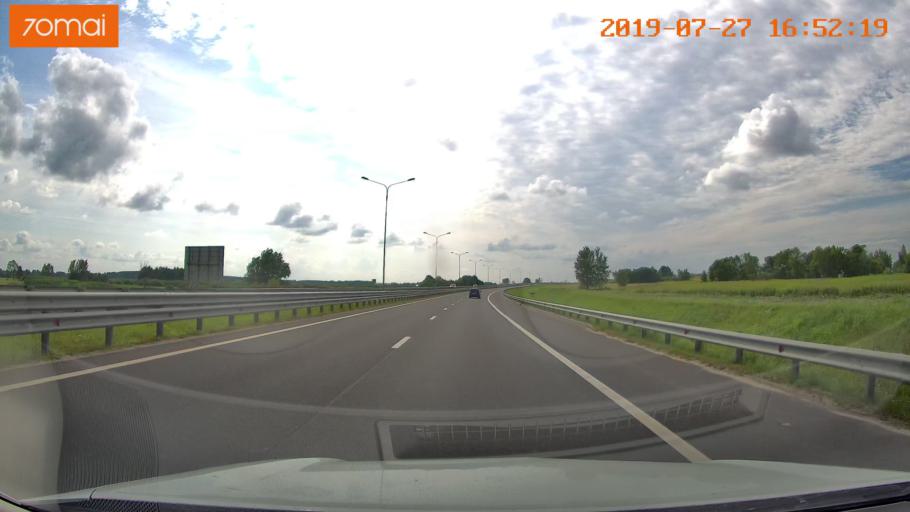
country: RU
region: Kaliningrad
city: Gvardeysk
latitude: 54.6838
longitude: 20.8630
